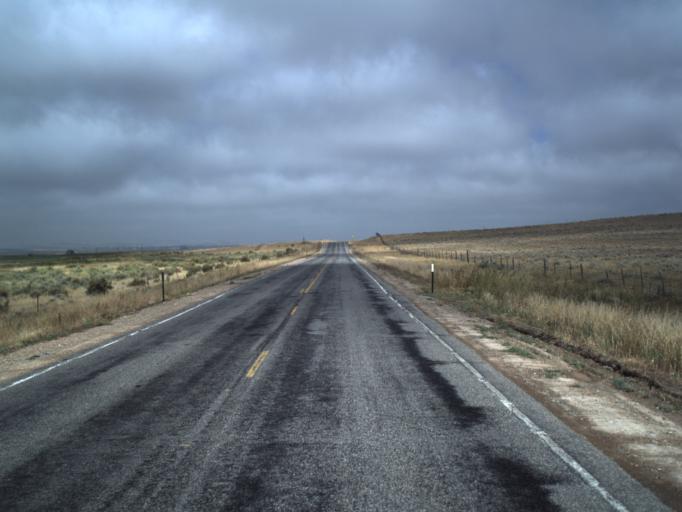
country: US
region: Utah
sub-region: Rich County
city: Randolph
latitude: 41.4749
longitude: -111.1109
